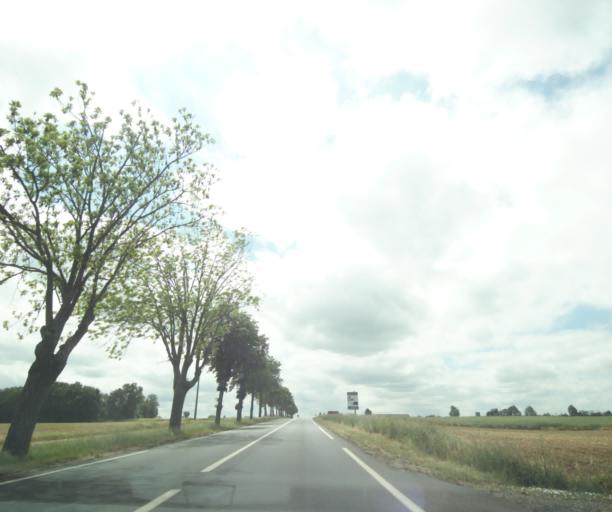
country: FR
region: Poitou-Charentes
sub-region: Departement des Deux-Sevres
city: Saint-Jean-de-Thouars
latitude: 46.9287
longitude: -0.1992
